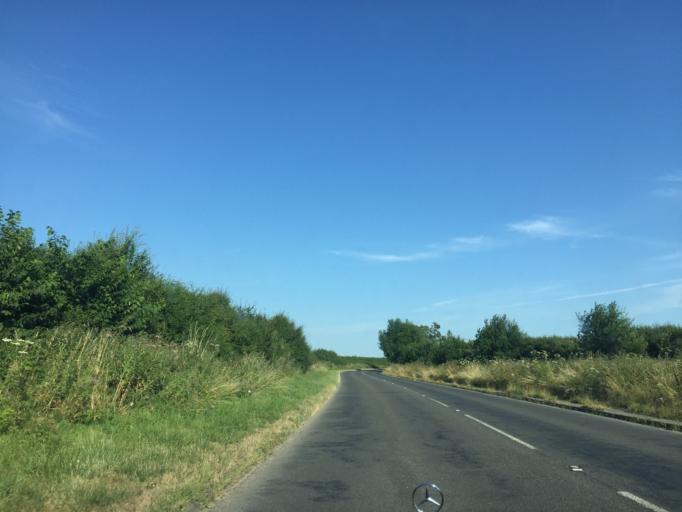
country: GB
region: England
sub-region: Oxfordshire
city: Thame
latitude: 51.7193
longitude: -1.0254
